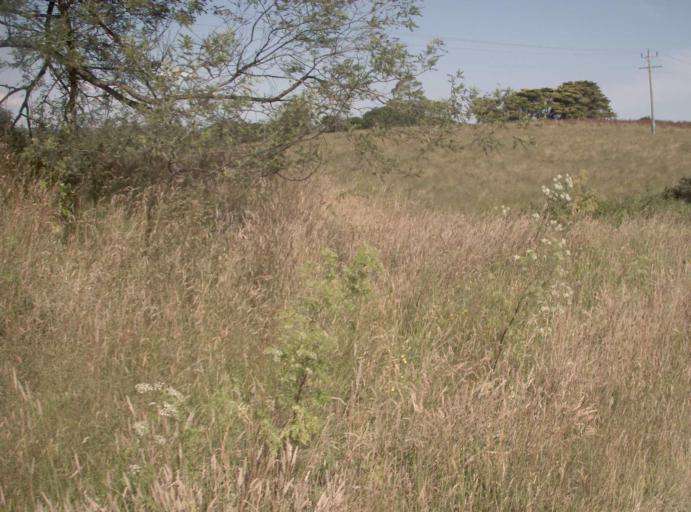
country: AU
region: Victoria
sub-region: Baw Baw
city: Warragul
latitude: -38.3536
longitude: 145.7846
